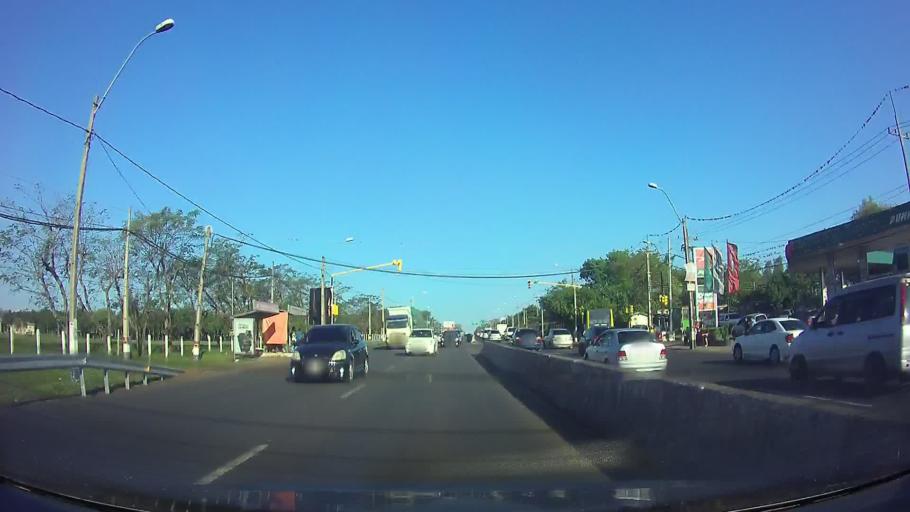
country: PY
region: Central
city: Capiata
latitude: -25.3602
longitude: -57.4323
